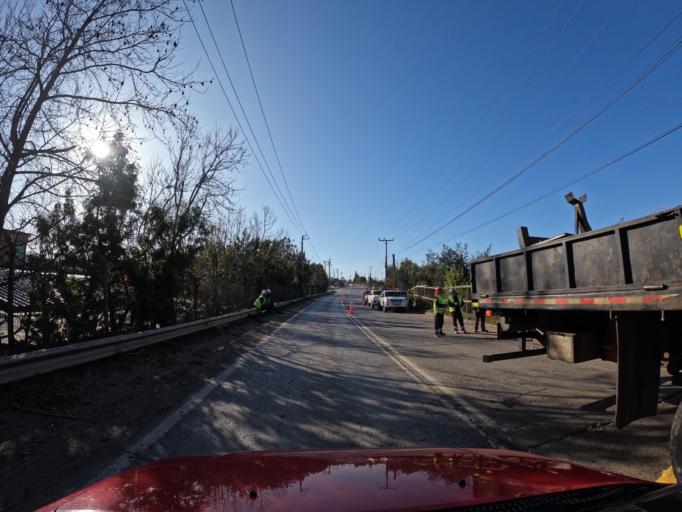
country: CL
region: Maule
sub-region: Provincia de Talca
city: Constitucion
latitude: -35.3727
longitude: -72.3965
